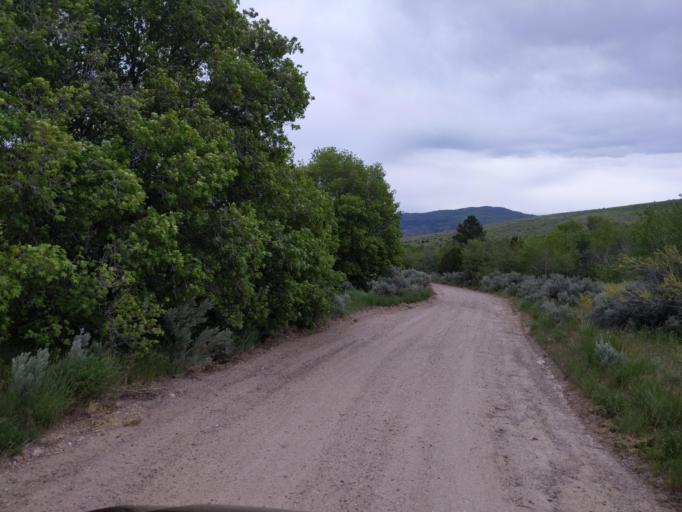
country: US
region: Idaho
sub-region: Bannock County
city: Pocatello
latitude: 42.8382
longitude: -112.4679
